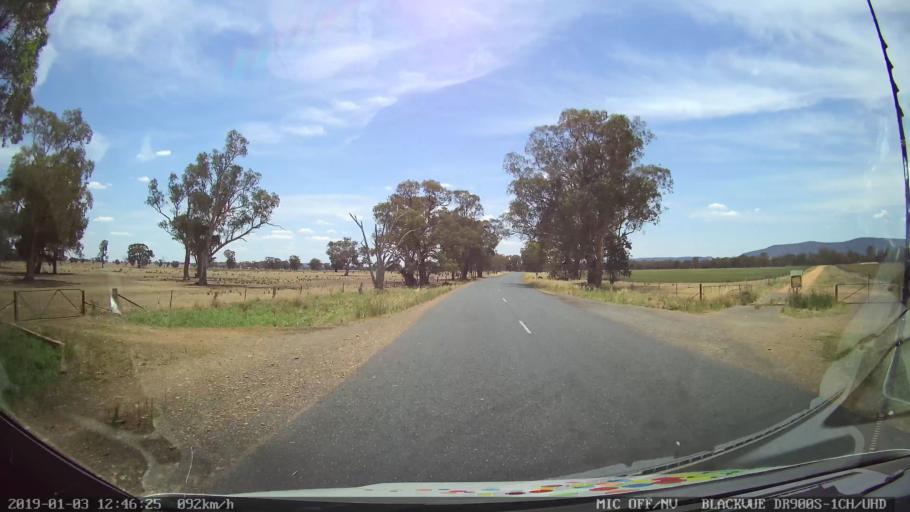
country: AU
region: New South Wales
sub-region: Weddin
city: Grenfell
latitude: -33.7384
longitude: 148.2332
